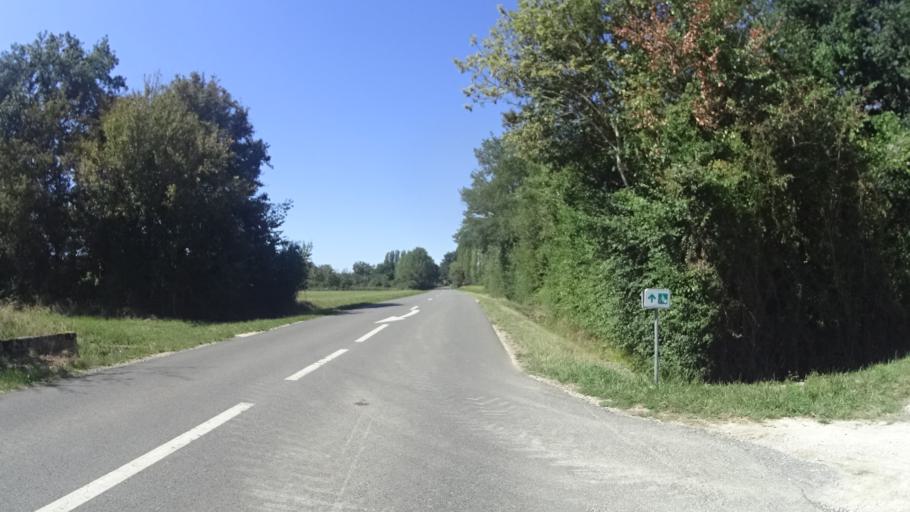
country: FR
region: Centre
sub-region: Departement du Cher
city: Belleville-sur-Loire
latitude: 47.5092
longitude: 2.8599
